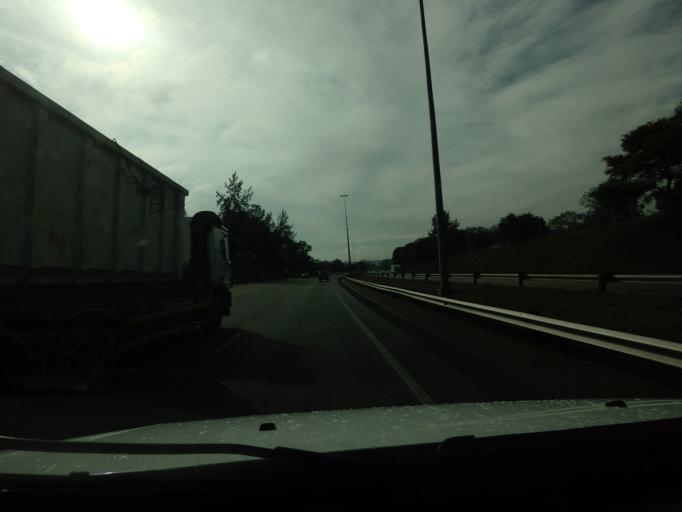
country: ZA
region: Gauteng
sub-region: City of Tshwane Metropolitan Municipality
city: Pretoria
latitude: -25.7419
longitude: 28.2870
